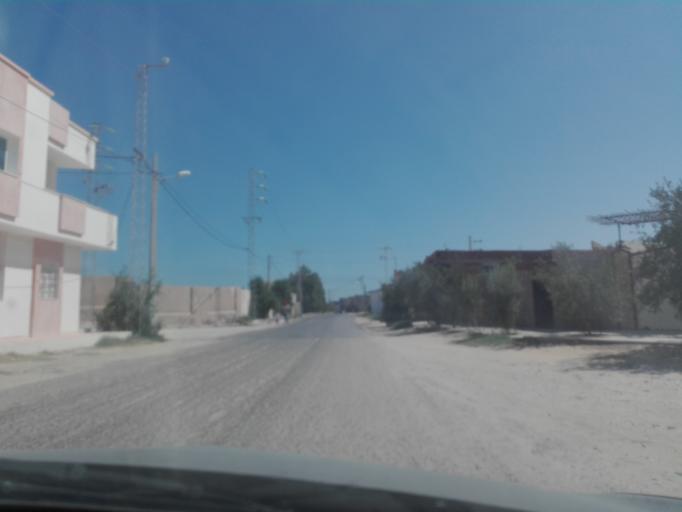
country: TN
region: Qabis
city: Gabes
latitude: 33.8695
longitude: 10.0493
